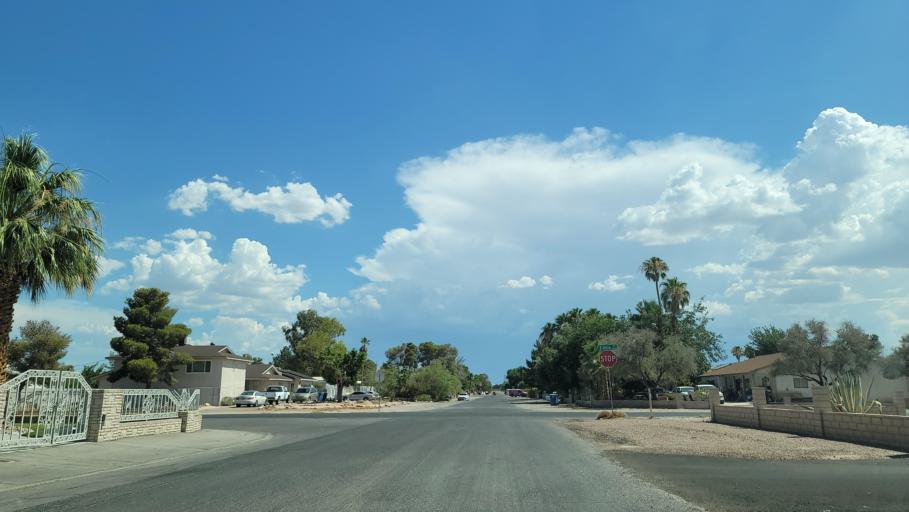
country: US
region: Nevada
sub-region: Clark County
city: Spring Valley
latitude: 36.1371
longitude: -115.2273
